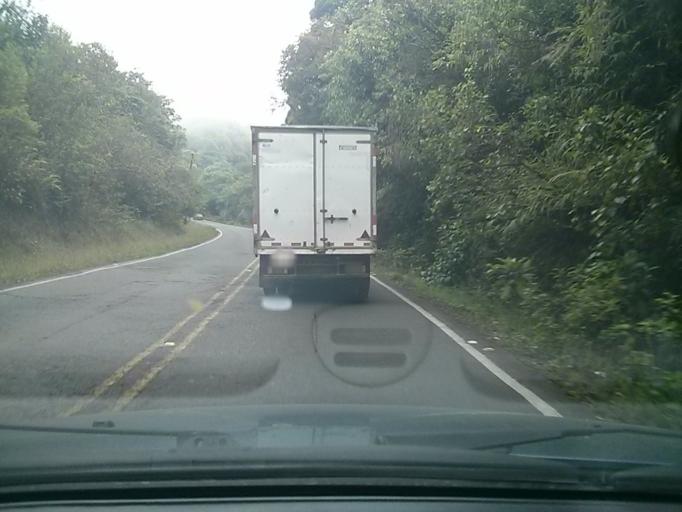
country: CR
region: San Jose
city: San Marcos
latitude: 9.7387
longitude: -83.9569
